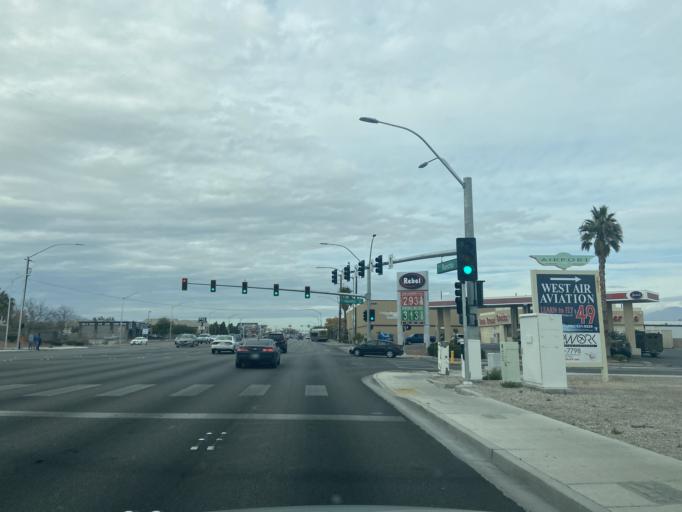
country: US
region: Nevada
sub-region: Clark County
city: Las Vegas
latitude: 36.2095
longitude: -115.2050
